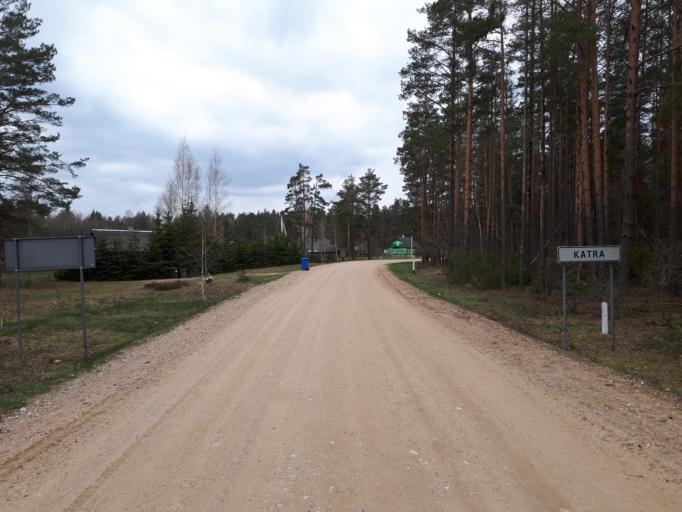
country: LT
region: Alytaus apskritis
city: Varena
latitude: 53.9959
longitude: 24.5962
